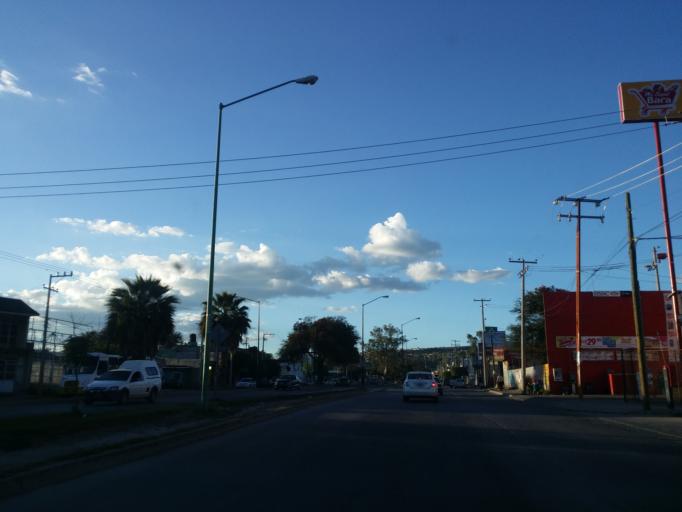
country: MX
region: Guanajuato
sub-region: Leon
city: Medina
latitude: 21.1908
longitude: -101.6648
